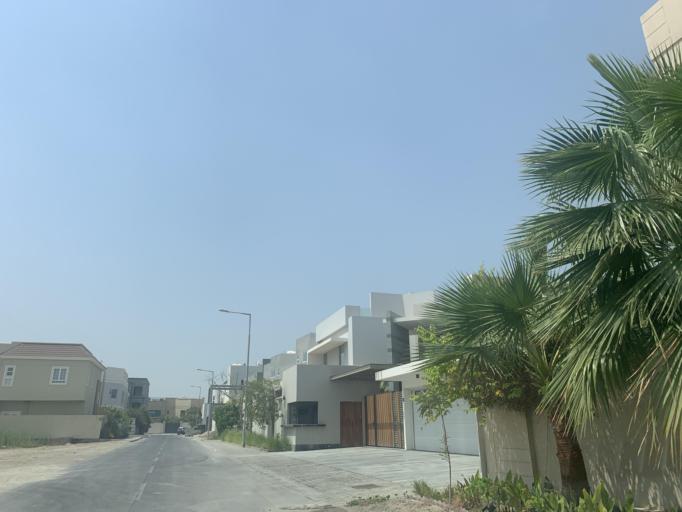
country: BH
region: Northern
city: Madinat `Isa
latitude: 26.1946
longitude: 50.4933
